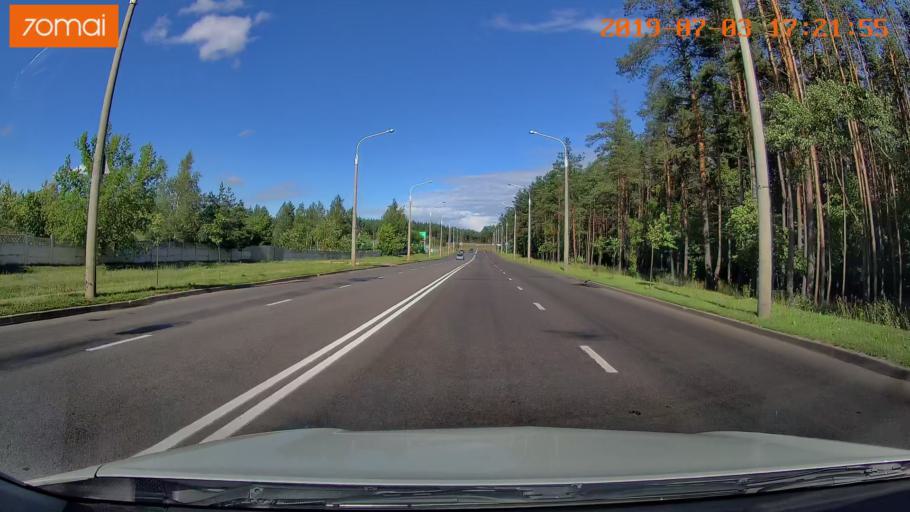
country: BY
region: Minsk
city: Vyaliki Trastsyanets
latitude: 53.9017
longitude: 27.6833
